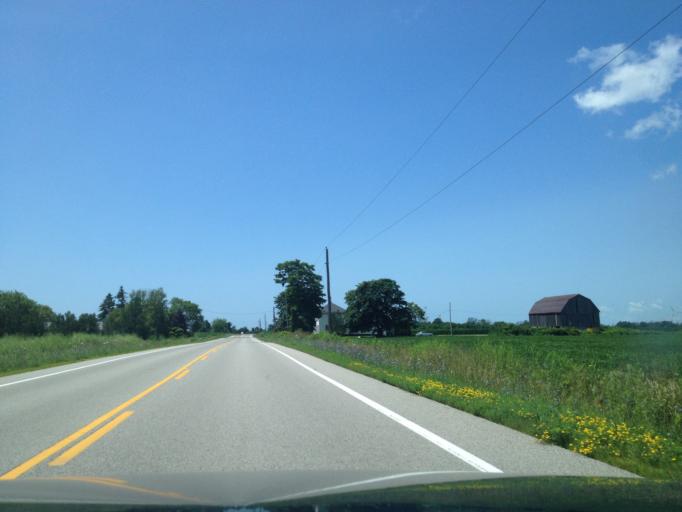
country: CA
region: Ontario
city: Norfolk County
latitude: 42.5772
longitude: -80.5353
